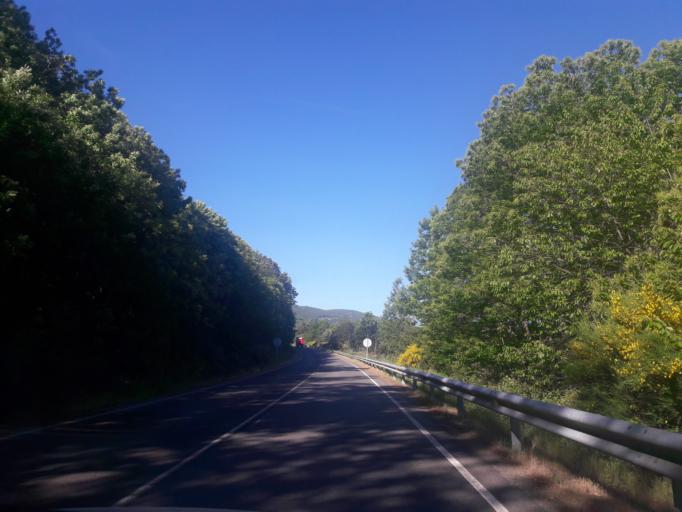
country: ES
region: Castille and Leon
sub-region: Provincia de Salamanca
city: Penacaballera
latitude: 40.3494
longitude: -5.8504
